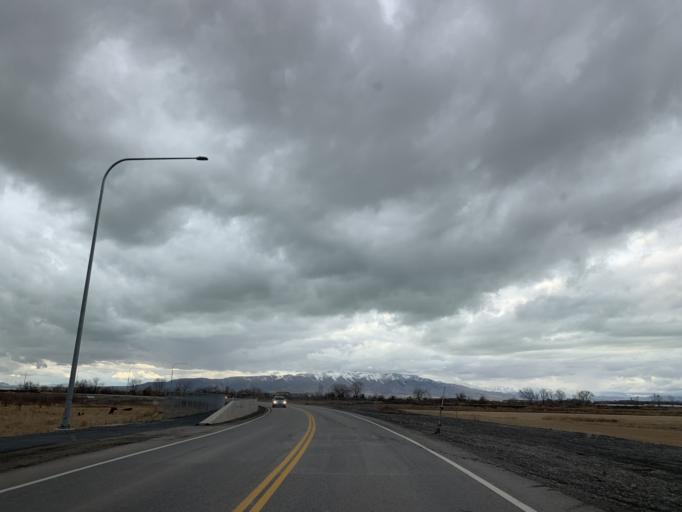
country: US
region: Utah
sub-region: Utah County
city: Provo
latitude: 40.2180
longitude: -111.6988
